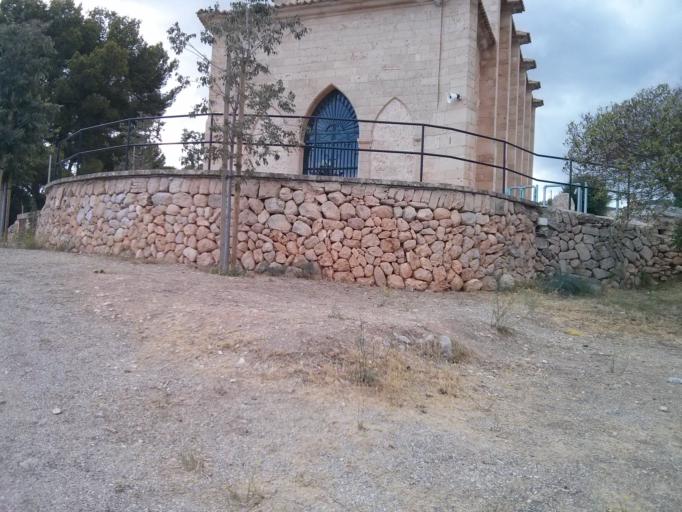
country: ES
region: Balearic Islands
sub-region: Illes Balears
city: Magaluf
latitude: 39.5324
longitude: 2.5742
